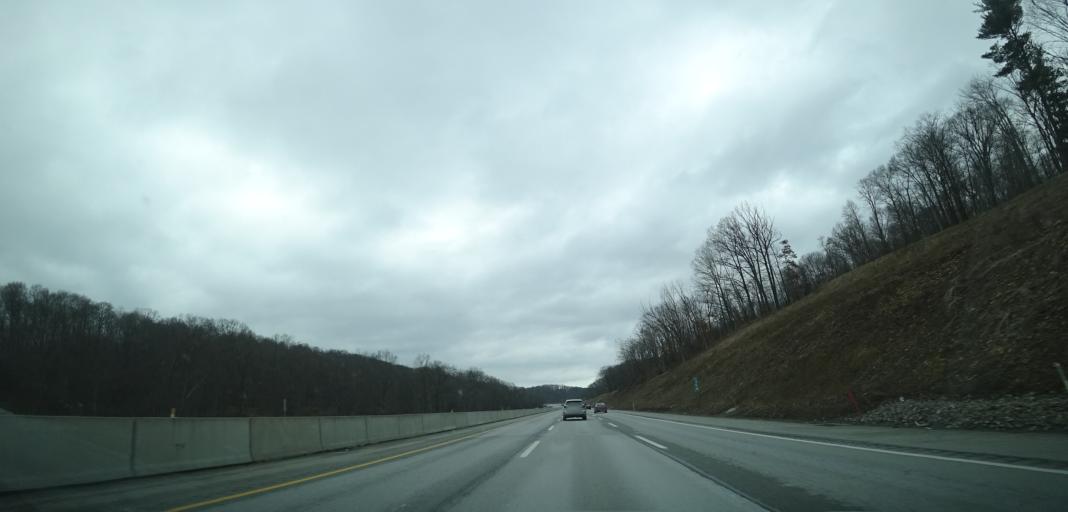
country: US
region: Pennsylvania
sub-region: Allegheny County
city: Gibsonia
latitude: 40.6340
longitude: -79.9889
